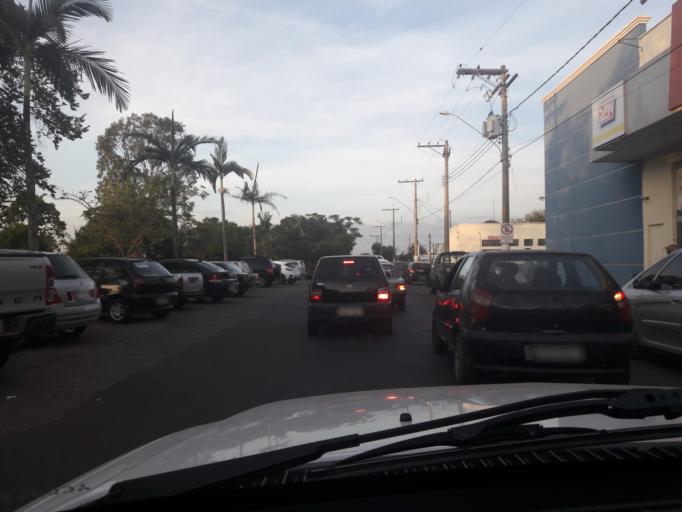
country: BR
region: Sao Paulo
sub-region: Moji-Guacu
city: Mogi-Gaucu
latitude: -22.3459
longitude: -46.9364
